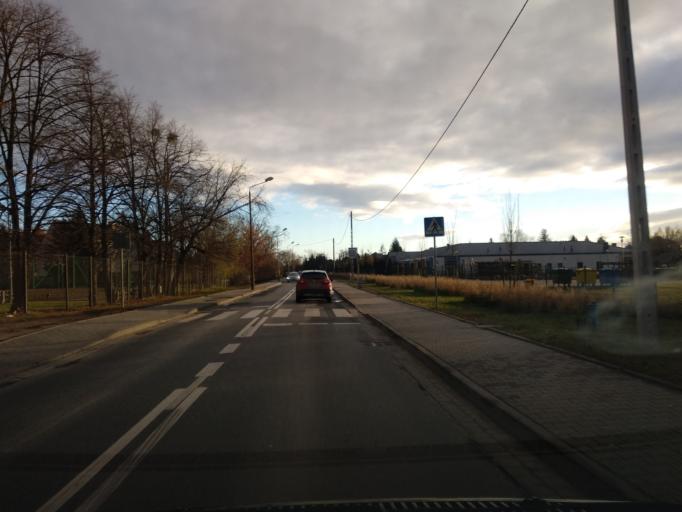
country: PL
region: Lower Silesian Voivodeship
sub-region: Powiat wroclawski
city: Zerniki Wroclawskie
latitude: 51.0555
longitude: 17.0263
